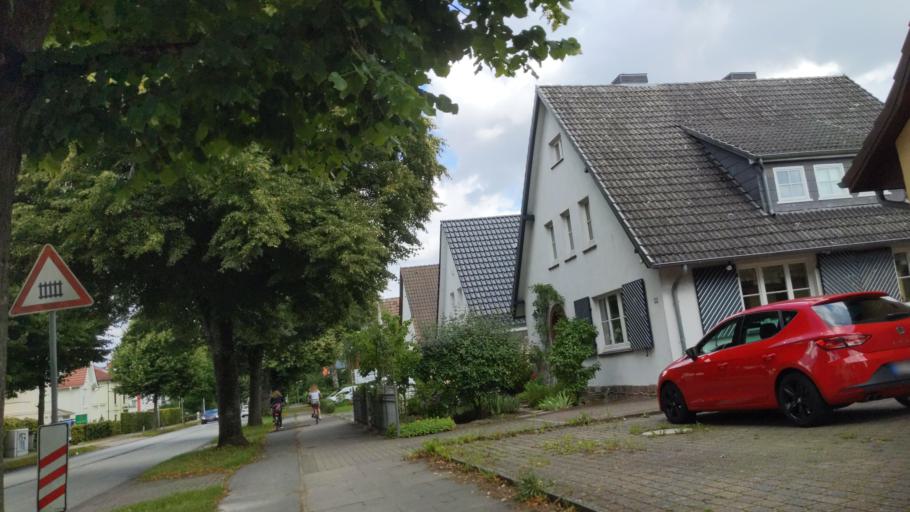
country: DE
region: Schleswig-Holstein
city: Bad Oldesloe
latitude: 53.8124
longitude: 10.3863
